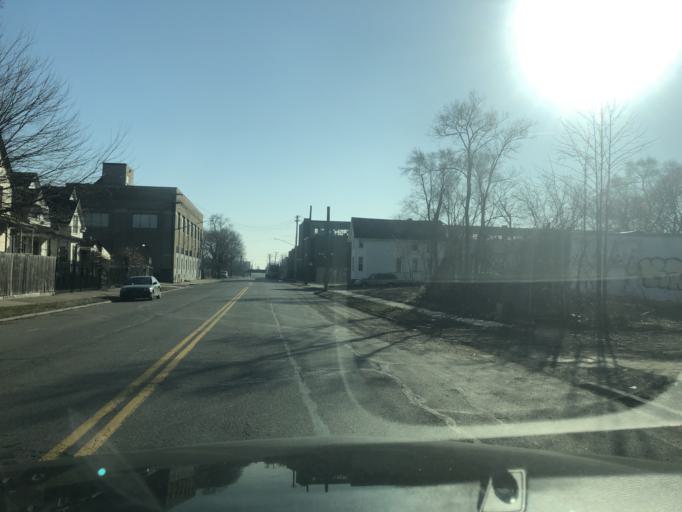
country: US
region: Michigan
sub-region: Wayne County
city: Detroit
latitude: 42.3350
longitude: -83.1040
